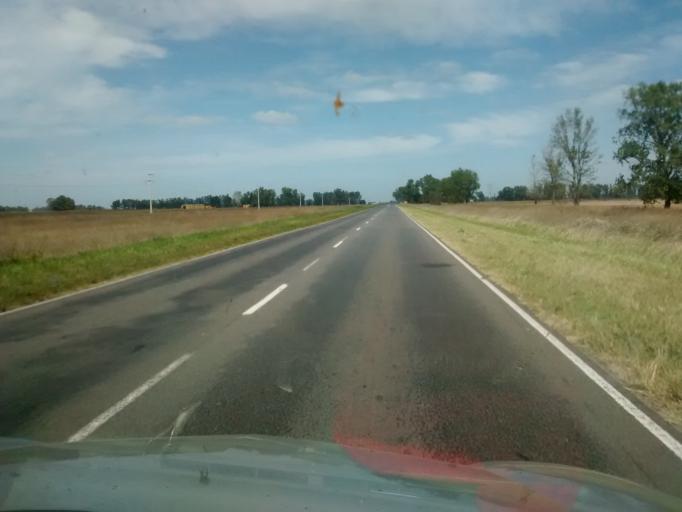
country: AR
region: Buenos Aires
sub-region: Partido de Ayacucho
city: Ayacucho
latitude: -37.1145
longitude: -58.5496
